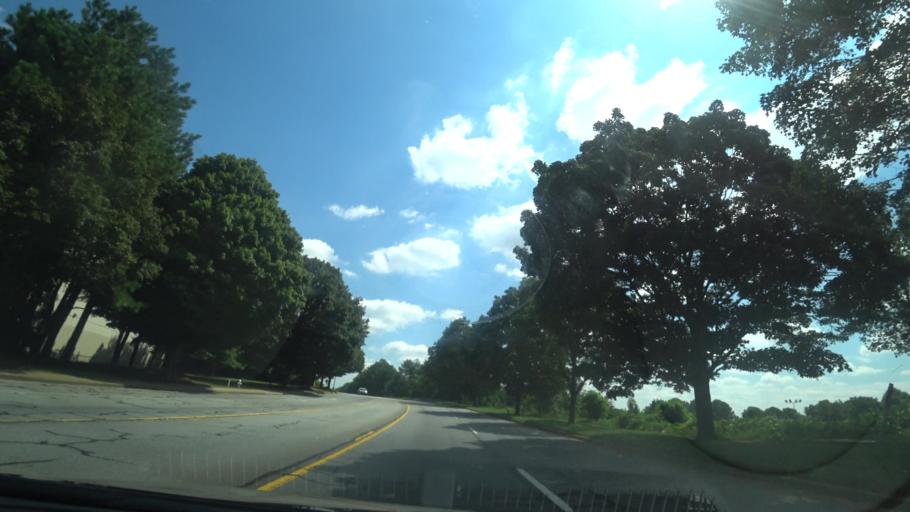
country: US
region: Georgia
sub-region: Gwinnett County
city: Norcross
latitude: 33.9197
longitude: -84.1963
